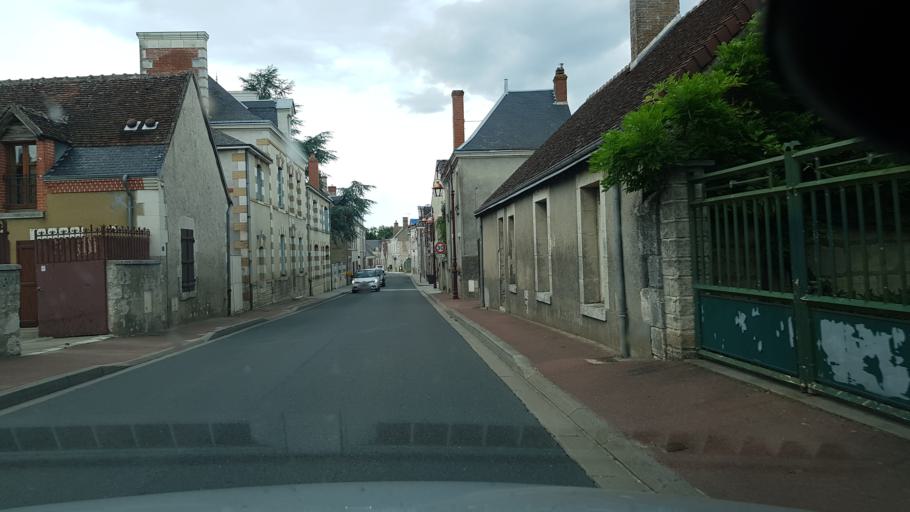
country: FR
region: Centre
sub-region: Departement du Loir-et-Cher
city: Chatillon-sur-Cher
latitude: 47.3437
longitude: 1.4794
